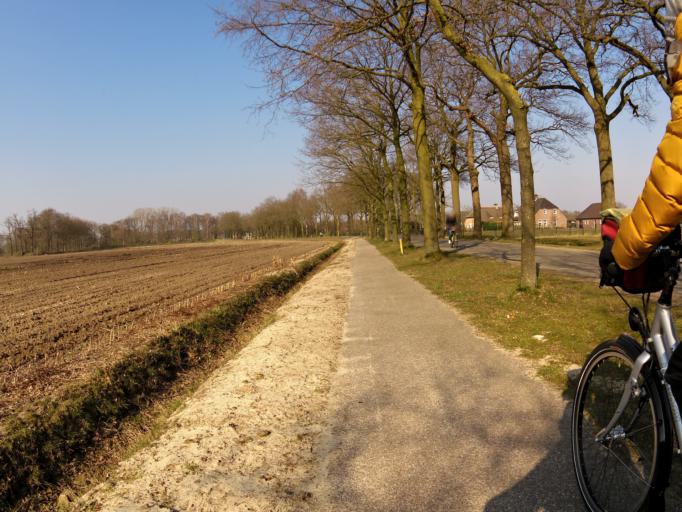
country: NL
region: North Brabant
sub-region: Gemeente Sint-Michielsgestel
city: Sint-Michielsgestel
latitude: 51.6979
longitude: 5.3854
